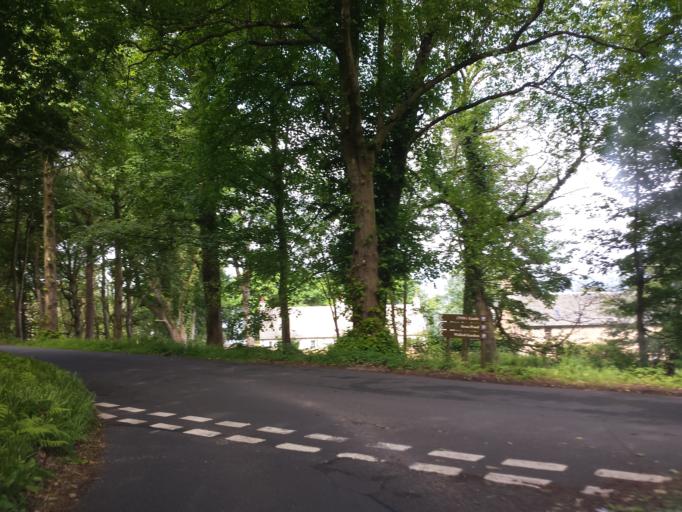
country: GB
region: Scotland
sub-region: South Ayrshire
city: Maybole
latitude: 55.3546
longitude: -4.7828
